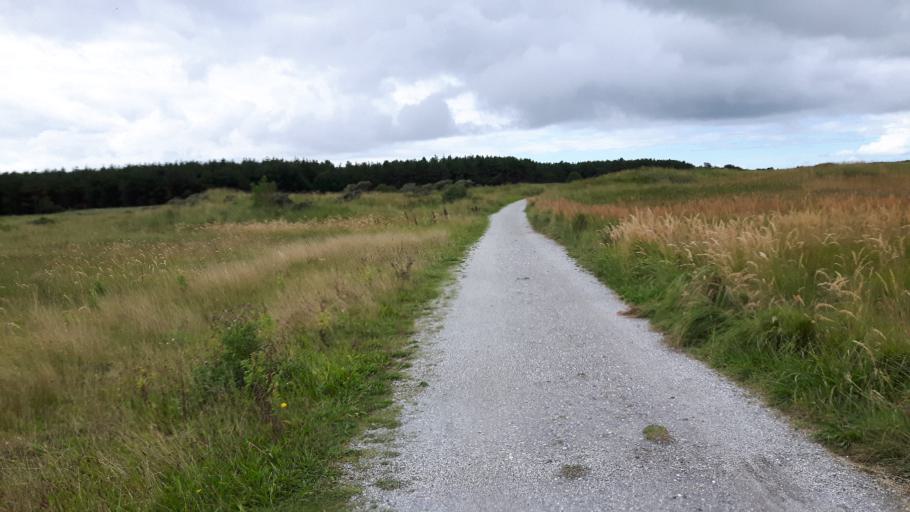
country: NL
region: Friesland
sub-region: Gemeente Ameland
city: Nes
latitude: 53.4547
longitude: 5.7161
